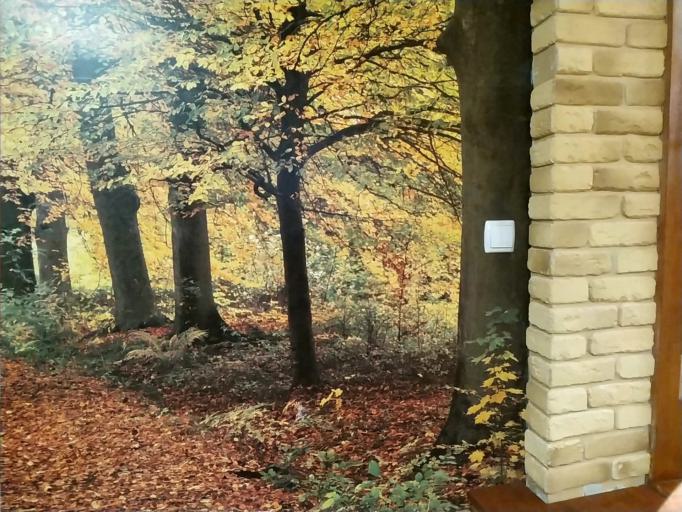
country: RU
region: Smolensk
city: Safonovo
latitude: 55.1982
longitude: 33.1831
